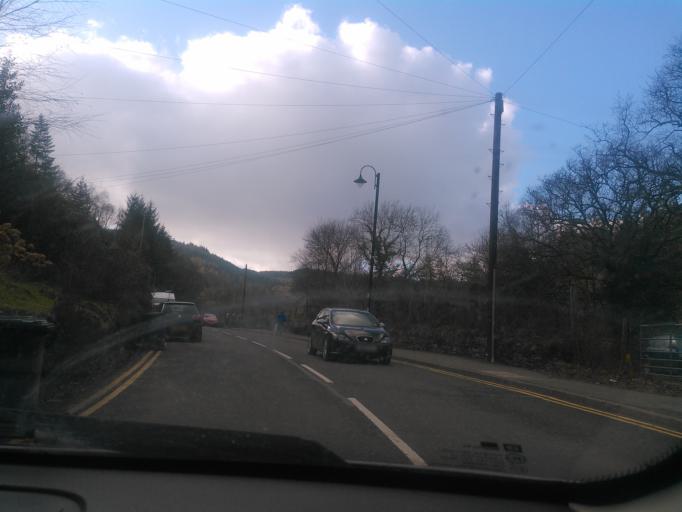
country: GB
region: Wales
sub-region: Conwy
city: Betws-y-Coed
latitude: 53.0940
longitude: -3.8083
